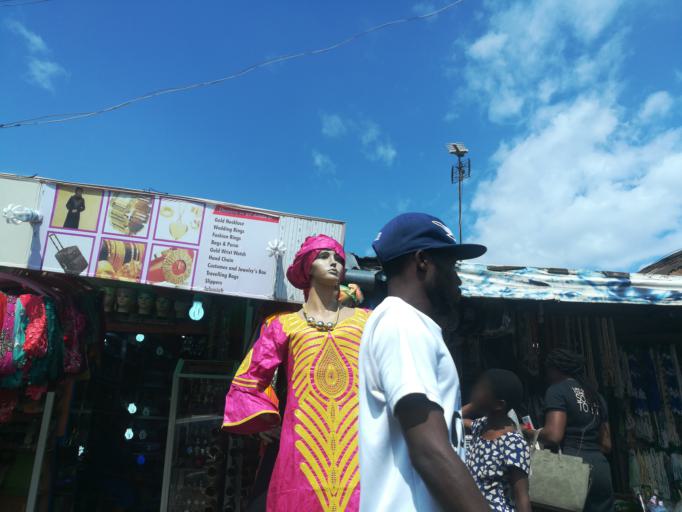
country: NG
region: Lagos
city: Agege
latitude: 6.6228
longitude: 3.3252
